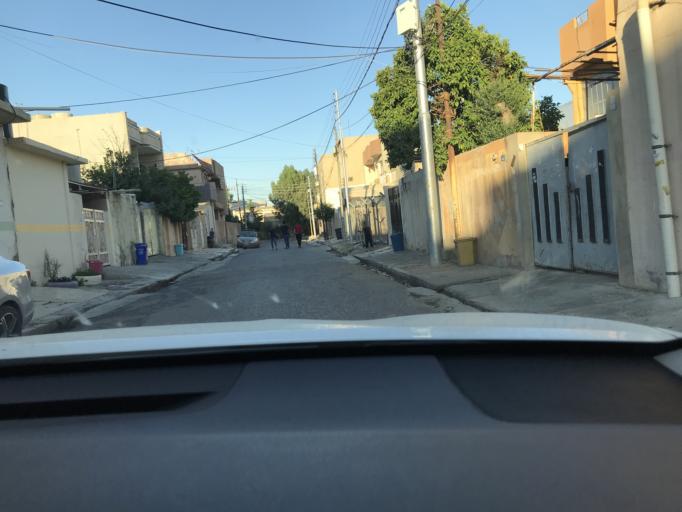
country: IQ
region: Arbil
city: Erbil
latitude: 36.2045
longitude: 44.0120
